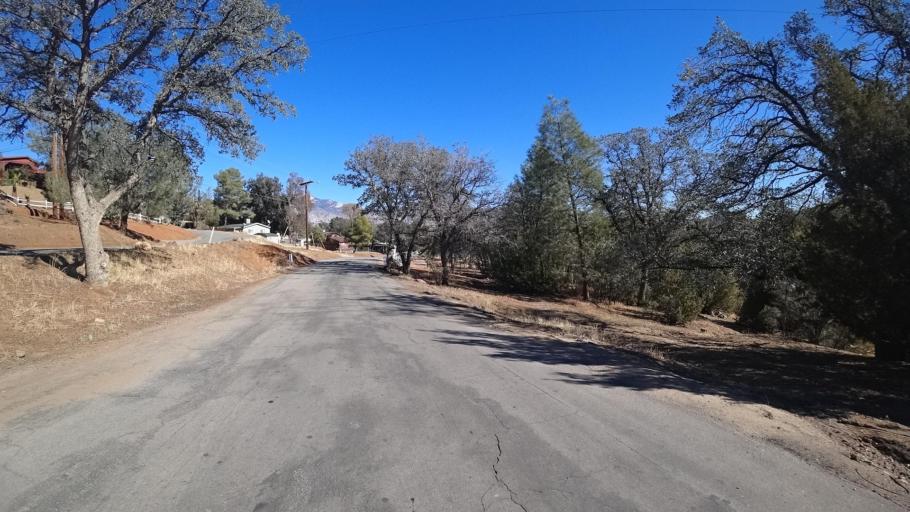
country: US
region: California
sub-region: Kern County
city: Wofford Heights
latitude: 35.7028
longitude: -118.4658
